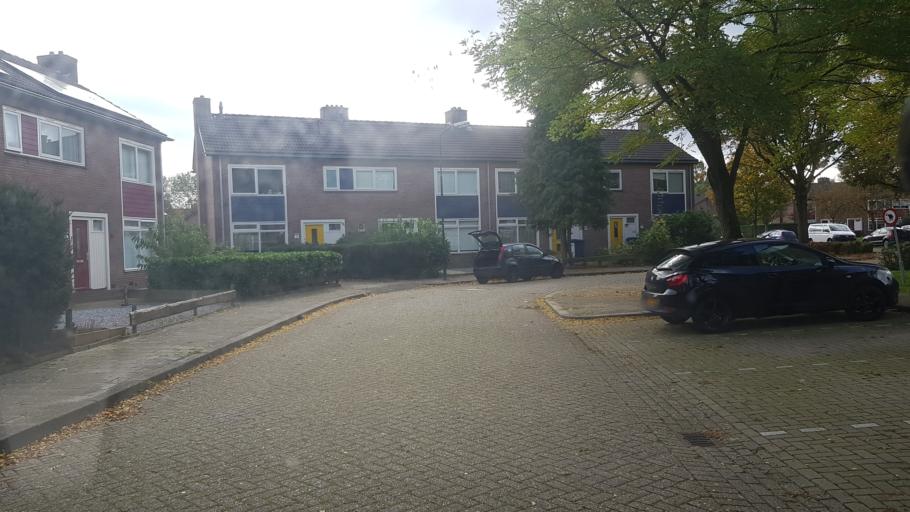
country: NL
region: Gelderland
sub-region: Gemeente Apeldoorn
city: Apeldoorn
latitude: 52.2019
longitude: 5.9407
